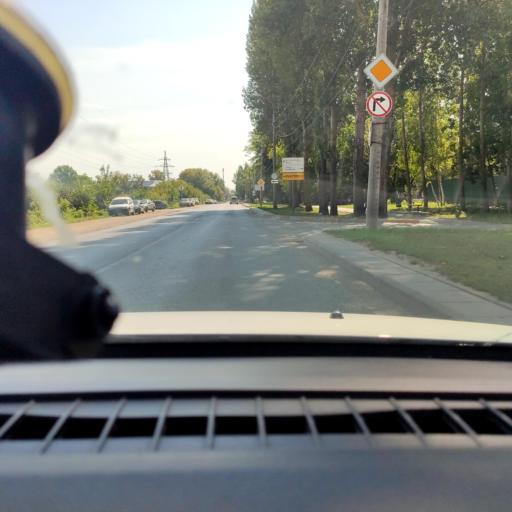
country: RU
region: Samara
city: Petra-Dubrava
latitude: 53.3061
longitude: 50.2795
